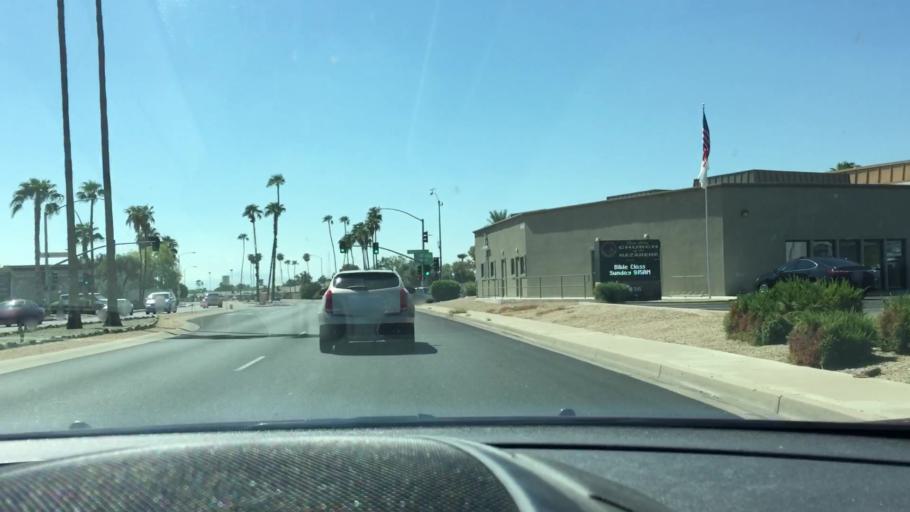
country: US
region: Arizona
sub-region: Maricopa County
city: Youngtown
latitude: 33.6183
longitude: -112.2914
